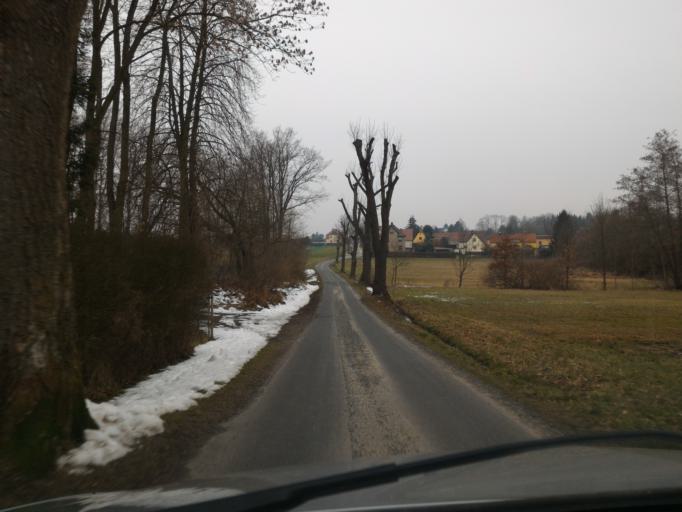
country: DE
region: Saxony
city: Neugersdorf
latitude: 50.9730
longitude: 14.6238
